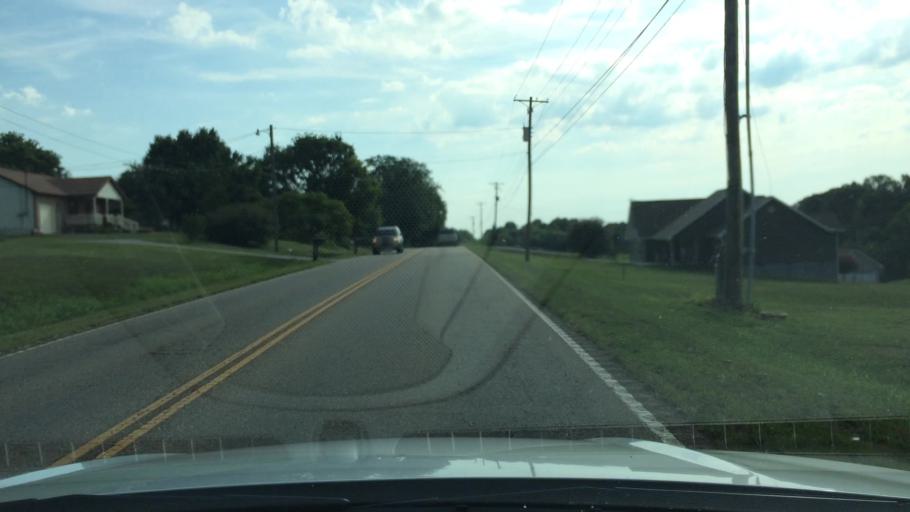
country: US
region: Tennessee
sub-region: Sevier County
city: Seymour
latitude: 35.8951
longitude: -83.7138
